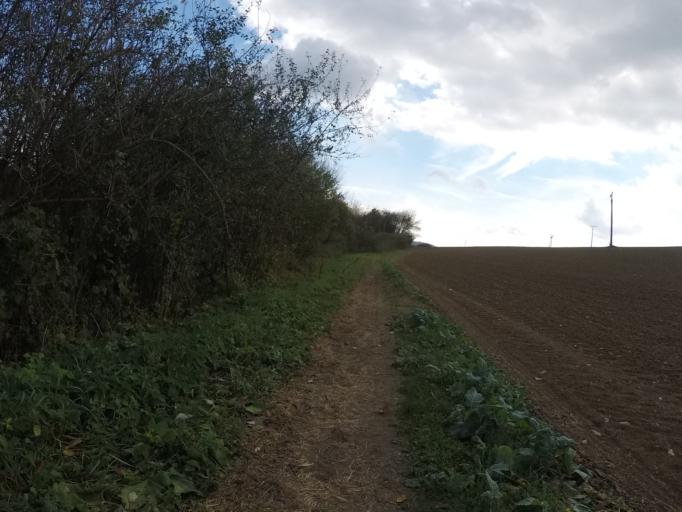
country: SK
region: Presovsky
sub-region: Okres Presov
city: Presov
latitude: 48.9311
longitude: 21.1815
